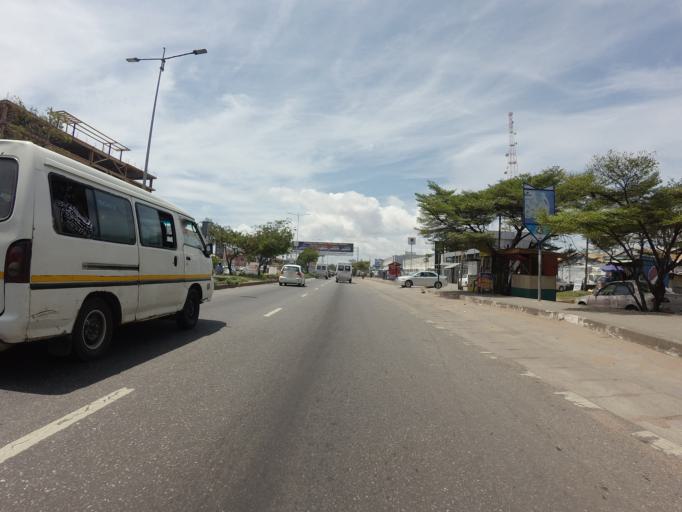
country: GH
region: Greater Accra
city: Accra
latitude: 5.5593
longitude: -0.2258
